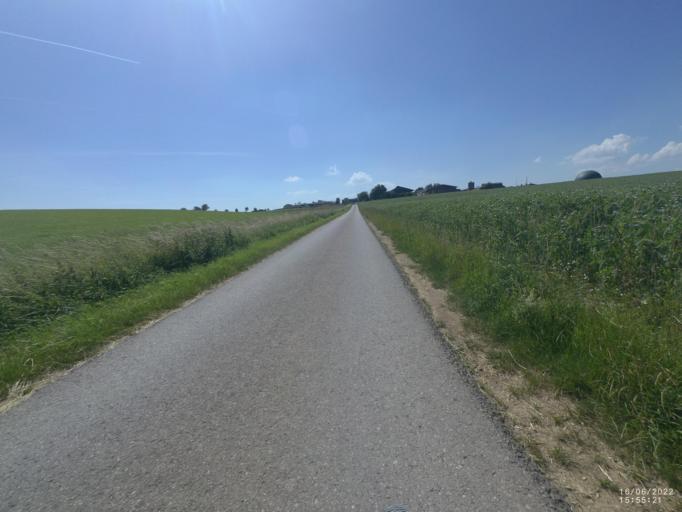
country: DE
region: Baden-Wuerttemberg
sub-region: Regierungsbezirk Stuttgart
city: Gerstetten
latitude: 48.6140
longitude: 10.0780
